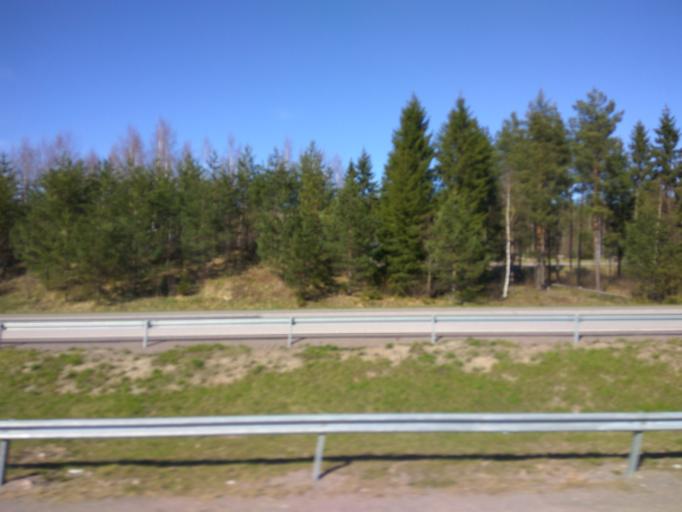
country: FI
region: Uusimaa
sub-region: Loviisa
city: Lovisa
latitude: 60.4608
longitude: 26.1537
